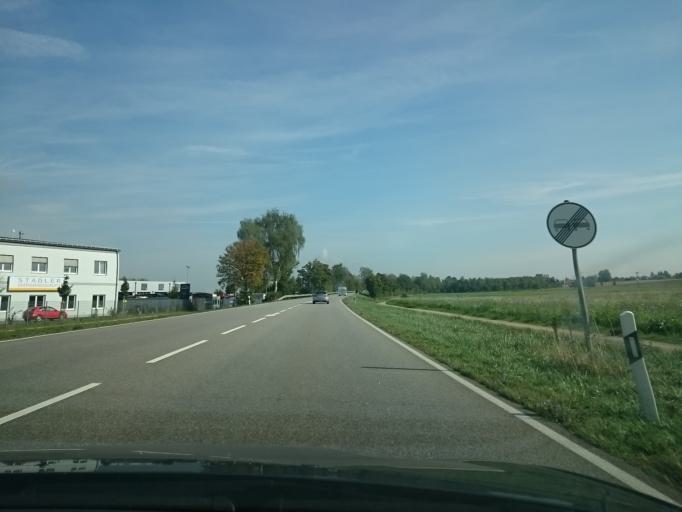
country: DE
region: Bavaria
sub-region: Upper Bavaria
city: Schrobenhausen
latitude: 48.5469
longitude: 11.2583
